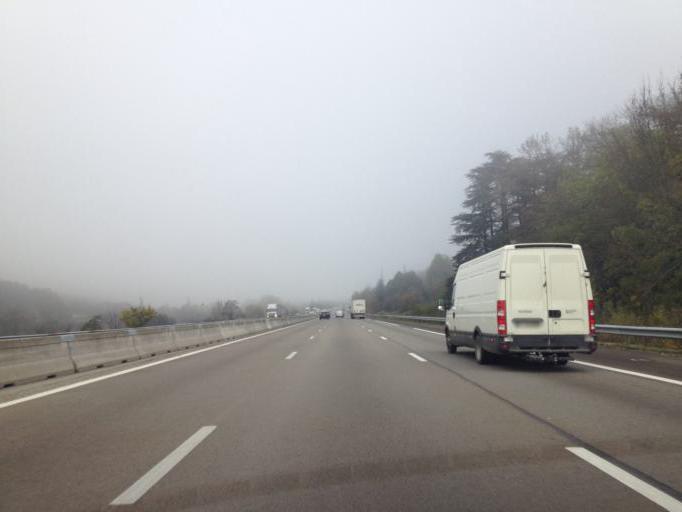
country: FR
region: Rhone-Alpes
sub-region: Departement de la Drome
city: Savasse
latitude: 44.6329
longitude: 4.7925
